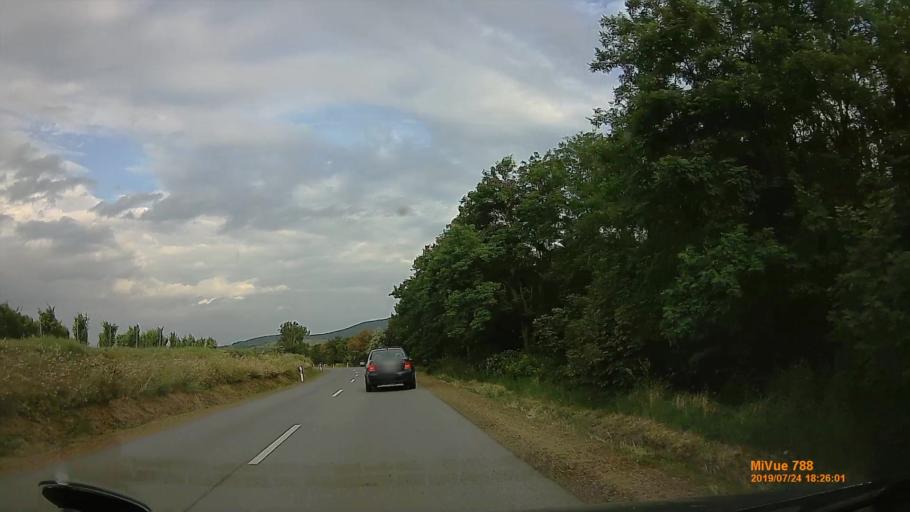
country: HU
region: Borsod-Abauj-Zemplen
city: Tarcal
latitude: 48.1451
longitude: 21.3244
